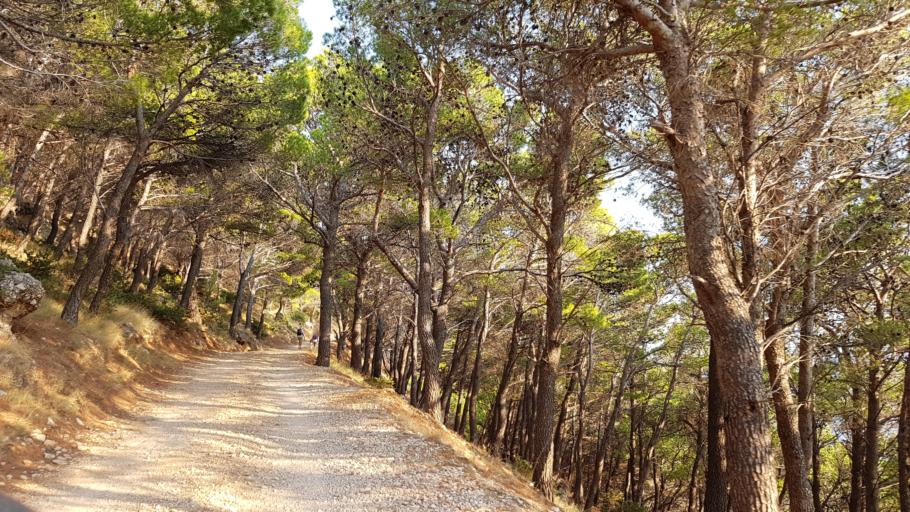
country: HR
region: Splitsko-Dalmatinska
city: Donja Brela
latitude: 43.3893
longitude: 16.8967
